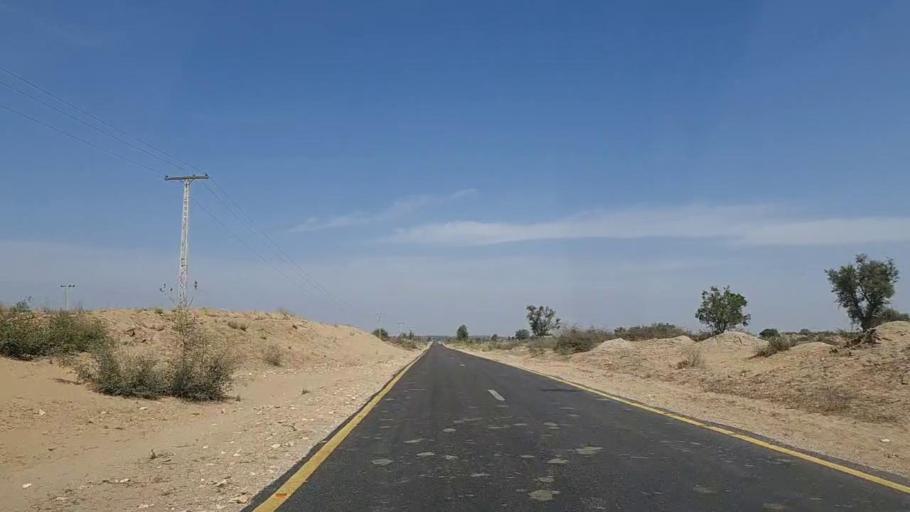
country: PK
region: Sindh
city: Mithi
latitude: 24.9537
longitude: 69.9040
